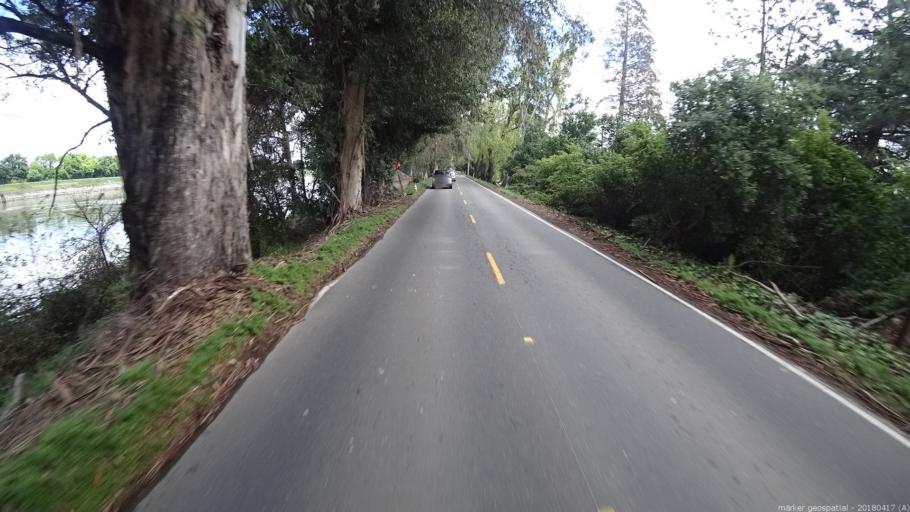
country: US
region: California
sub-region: Solano County
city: Rio Vista
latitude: 38.1729
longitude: -121.5918
